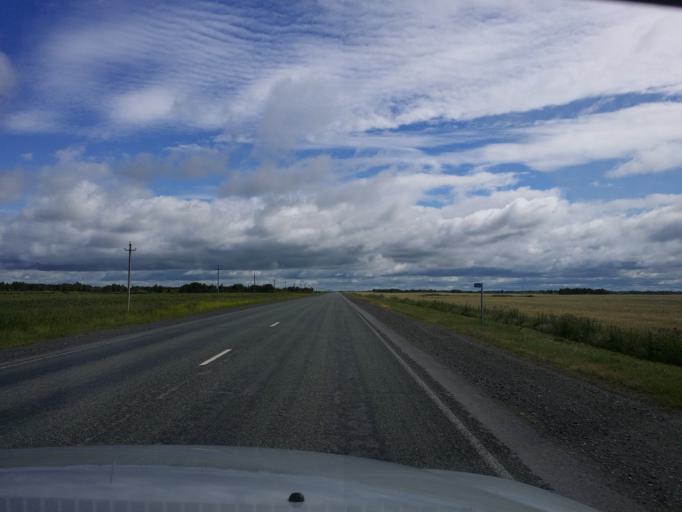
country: RU
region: Tjumen
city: Yarkovo
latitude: 57.2899
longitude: 66.9006
